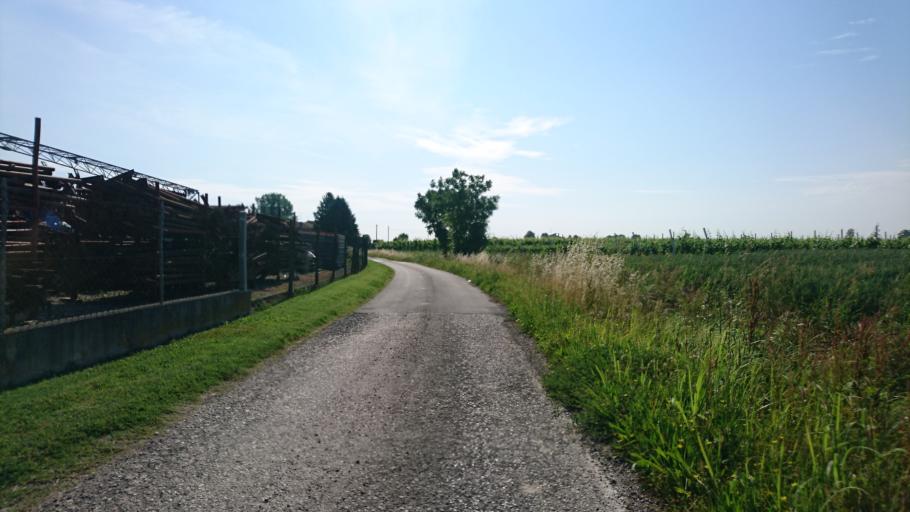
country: IT
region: Veneto
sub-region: Provincia di Verona
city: Terrazzo
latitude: 45.1730
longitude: 11.4163
